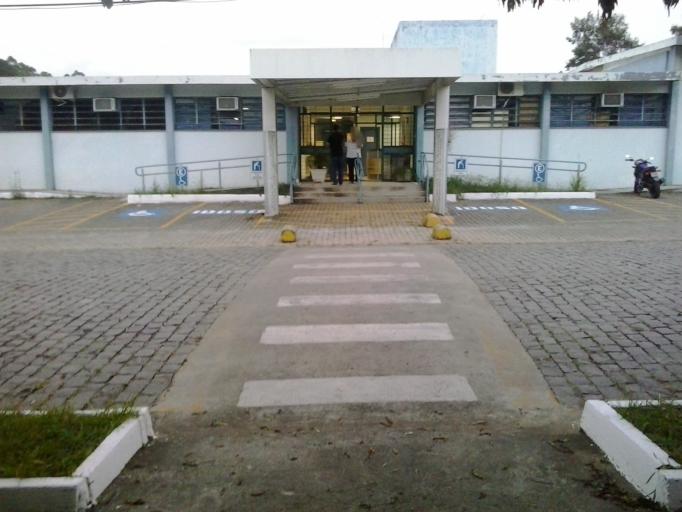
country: BR
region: Rio Grande do Sul
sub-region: Santa Maria
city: Santa Maria
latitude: -29.7167
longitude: -53.7185
